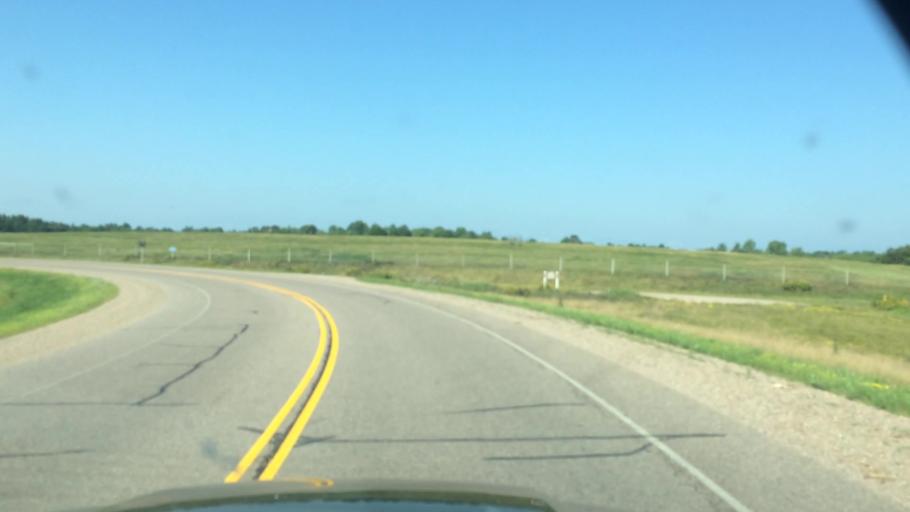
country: US
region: Wisconsin
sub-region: Langlade County
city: Antigo
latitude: 45.1620
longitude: -89.1608
